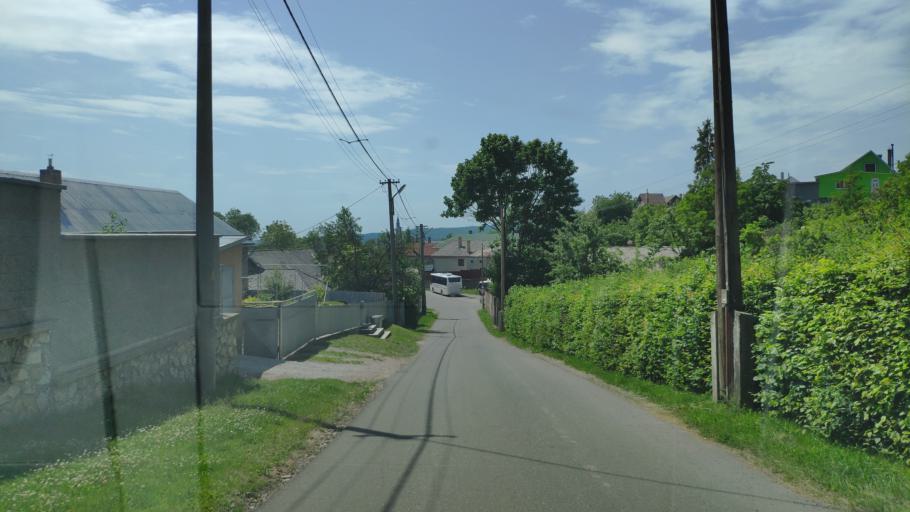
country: SK
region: Kosicky
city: Medzev
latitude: 48.7155
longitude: 20.9758
